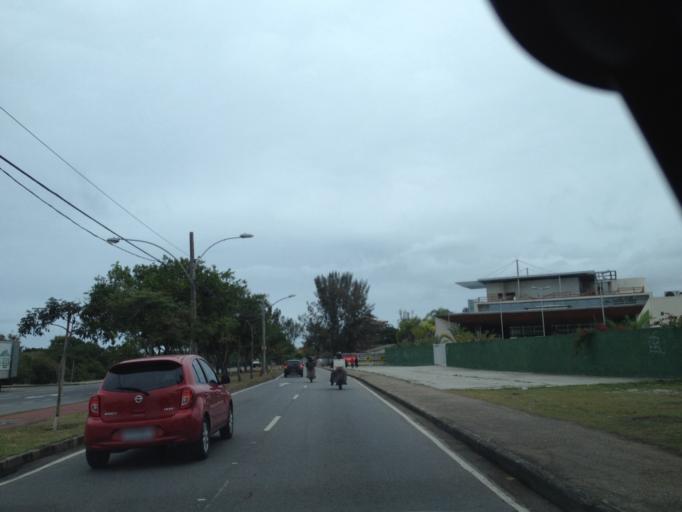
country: BR
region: Rio de Janeiro
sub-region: Nilopolis
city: Nilopolis
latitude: -23.0121
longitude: -43.4438
